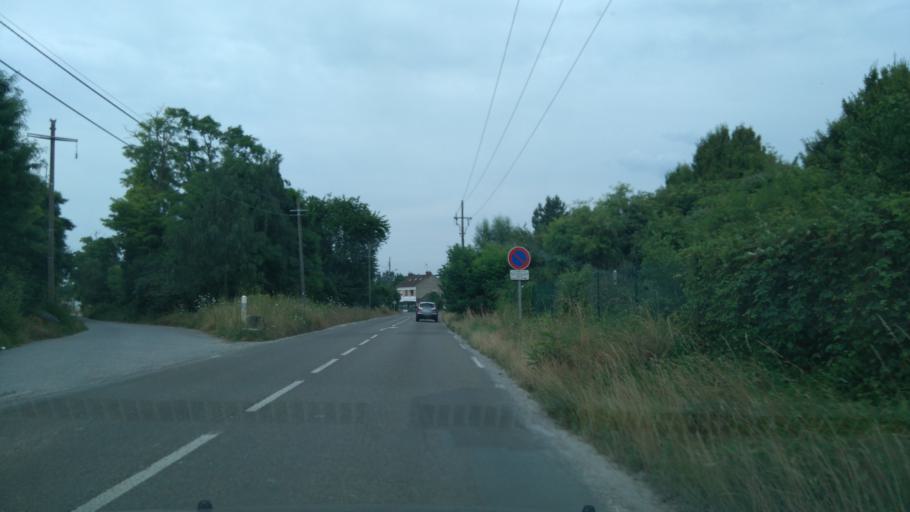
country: FR
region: Picardie
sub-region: Departement de l'Oise
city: Saint-Maximin
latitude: 49.2154
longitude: 2.4490
